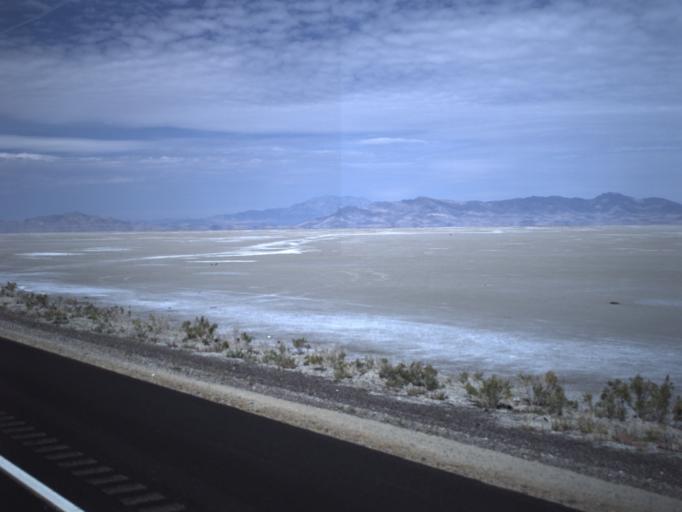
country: US
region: Utah
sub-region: Tooele County
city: Wendover
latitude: 40.7339
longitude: -113.5913
